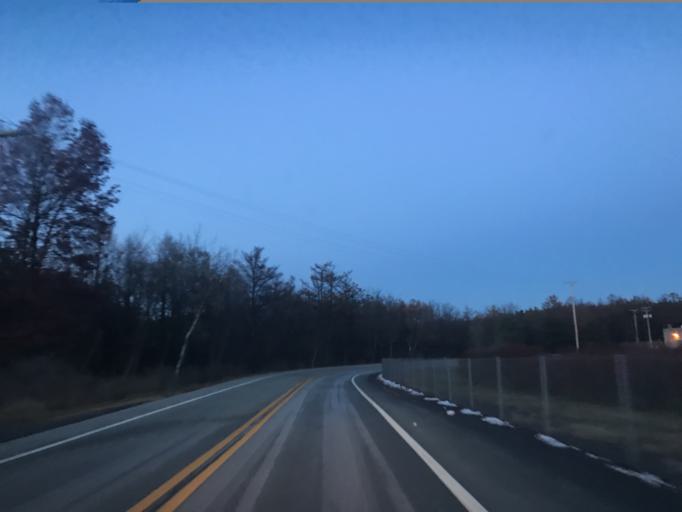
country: US
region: Pennsylvania
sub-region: Fulton County
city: McConnellsburg
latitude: 40.0600
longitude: -78.0840
